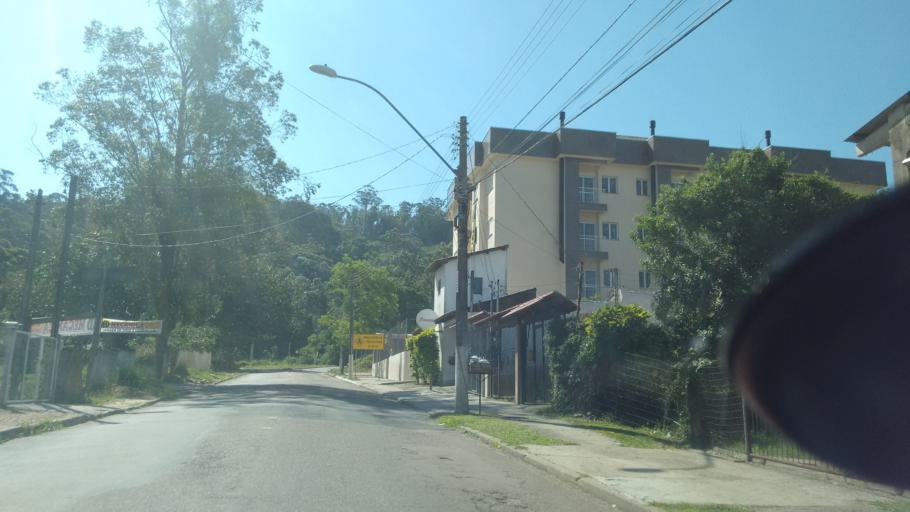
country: BR
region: Rio Grande do Sul
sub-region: Viamao
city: Viamao
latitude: -30.0564
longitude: -51.1048
